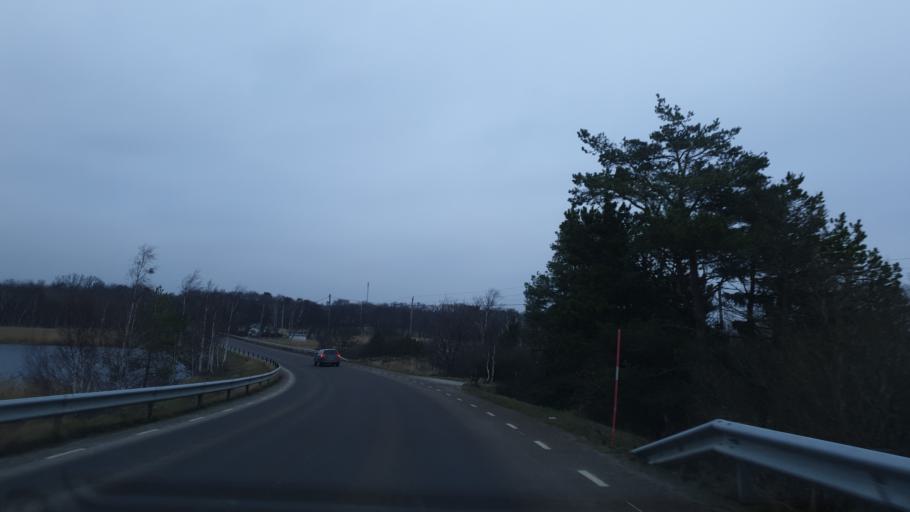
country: SE
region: Blekinge
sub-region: Karlskrona Kommun
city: Sturko
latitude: 56.1186
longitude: 15.7334
